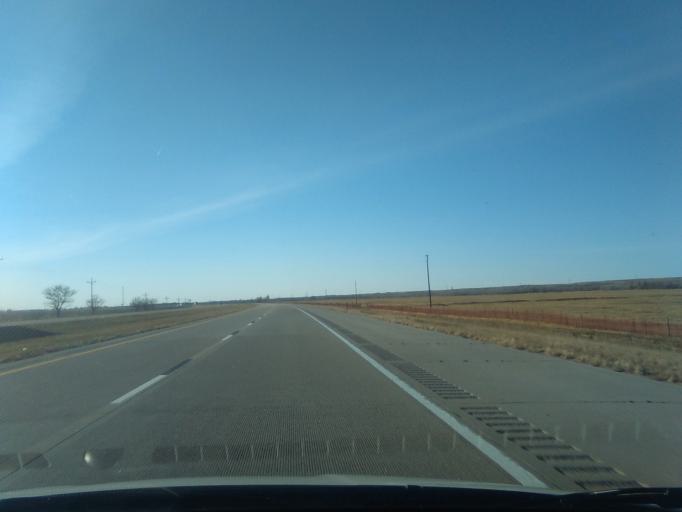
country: US
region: Colorado
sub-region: Sedgwick County
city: Julesburg
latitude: 41.0626
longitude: -102.0147
